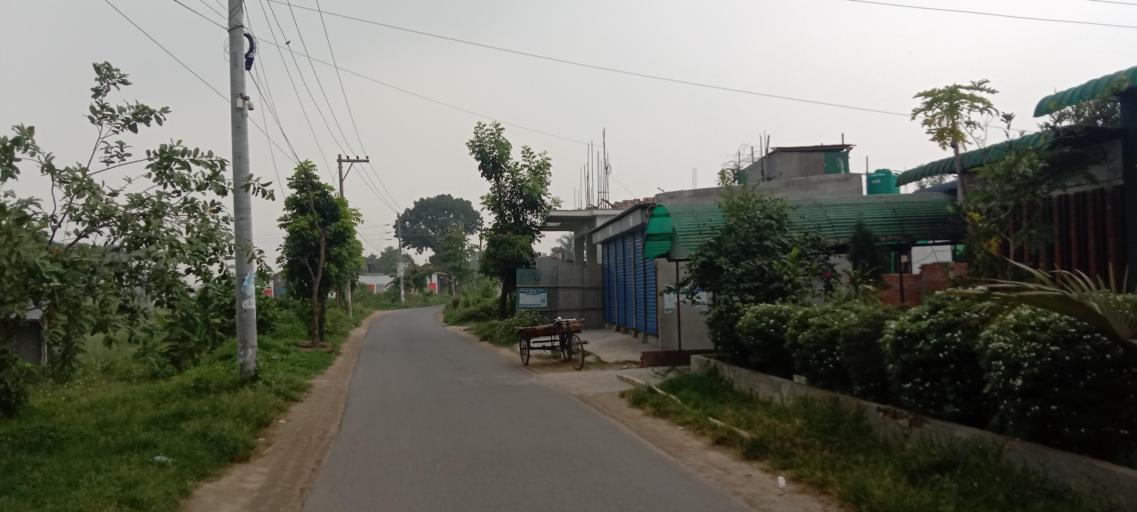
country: BD
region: Dhaka
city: Azimpur
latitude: 23.7385
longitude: 90.3182
